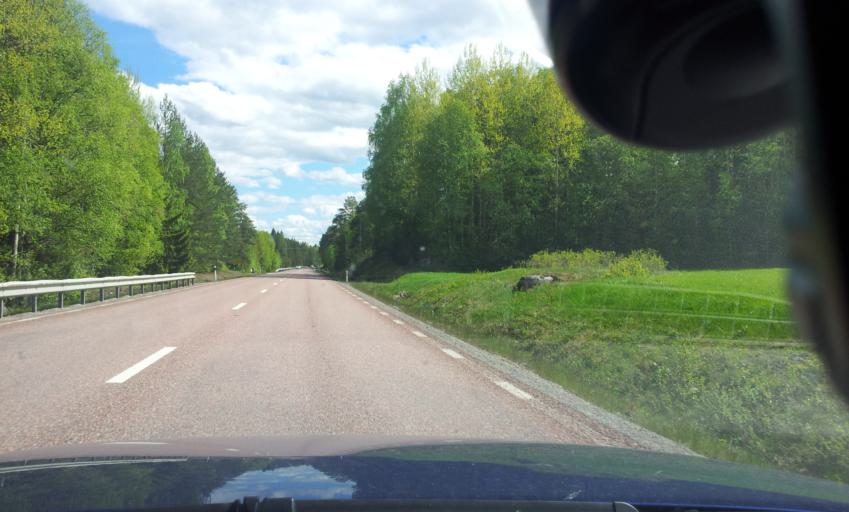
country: SE
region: Gaevleborg
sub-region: Ljusdals Kommun
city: Ljusdal
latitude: 61.7985
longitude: 16.1194
